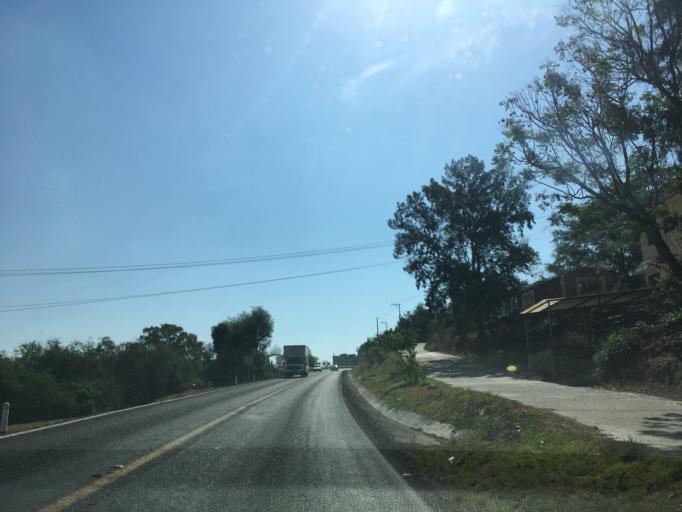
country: MX
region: Michoacan
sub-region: Morelia
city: Fraccionamiento Mision del Valle
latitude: 19.7379
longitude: -101.0996
